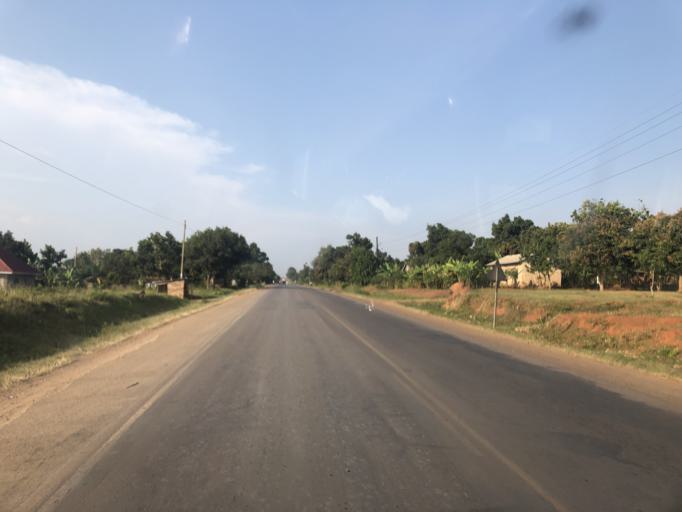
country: UG
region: Central Region
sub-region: Butambala District
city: Gombe
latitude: 0.0701
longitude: 32.1161
